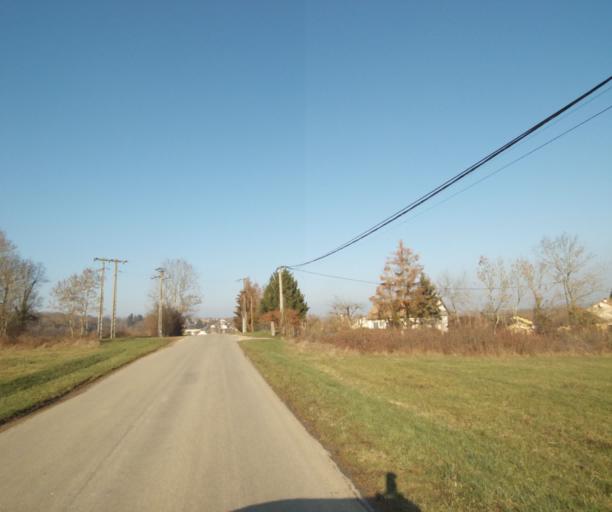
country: FR
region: Champagne-Ardenne
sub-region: Departement de la Haute-Marne
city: Wassy
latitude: 48.5090
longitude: 4.9213
